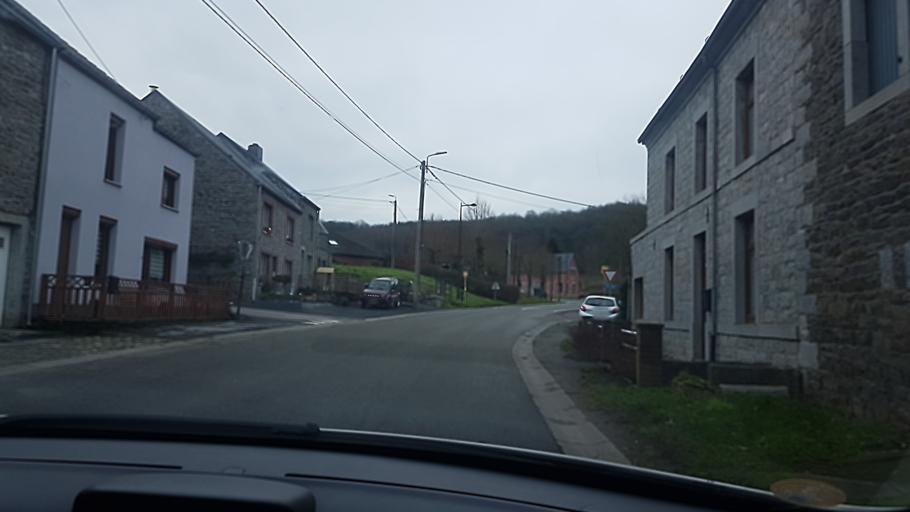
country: BE
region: Wallonia
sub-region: Province de Namur
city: Couvin
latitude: 50.0665
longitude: 4.6079
